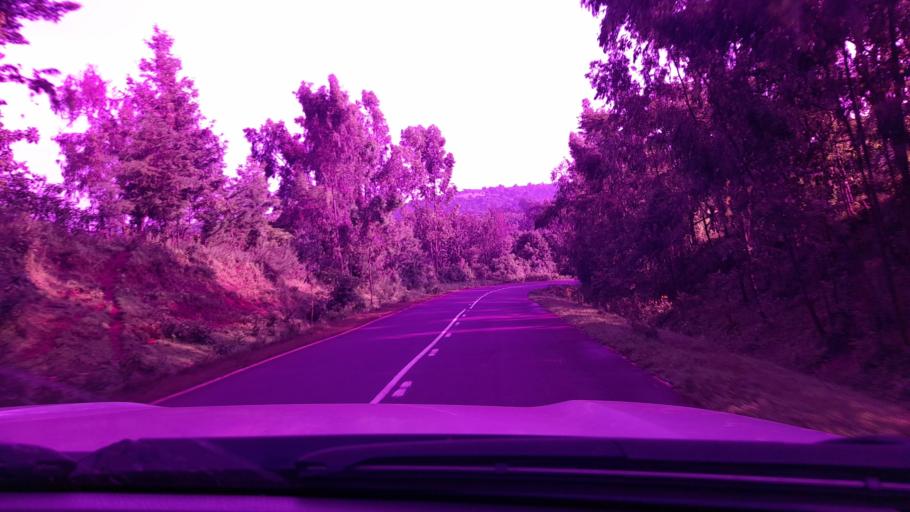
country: ET
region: Oromiya
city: Bedele
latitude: 8.1371
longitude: 36.4512
